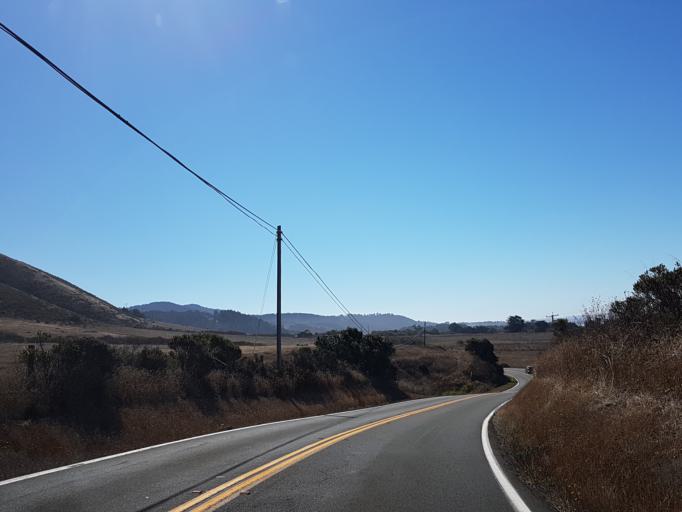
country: US
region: California
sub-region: Mendocino County
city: Boonville
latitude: 39.0765
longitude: -123.6944
